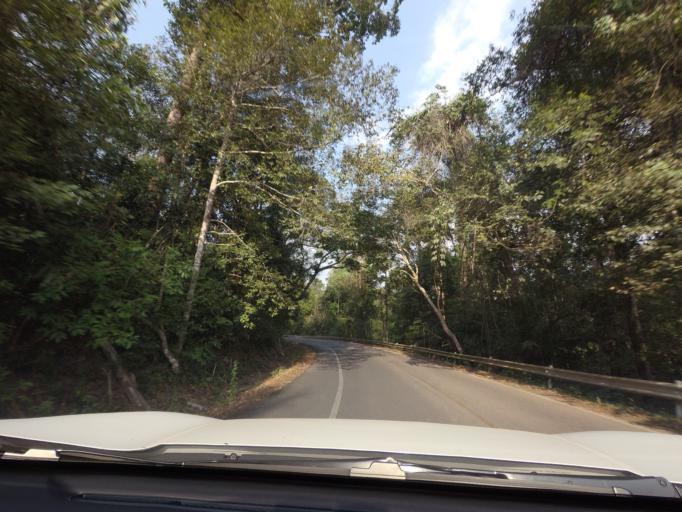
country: TH
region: Nakhon Nayok
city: Nakhon Nayok
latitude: 14.4206
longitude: 101.3886
